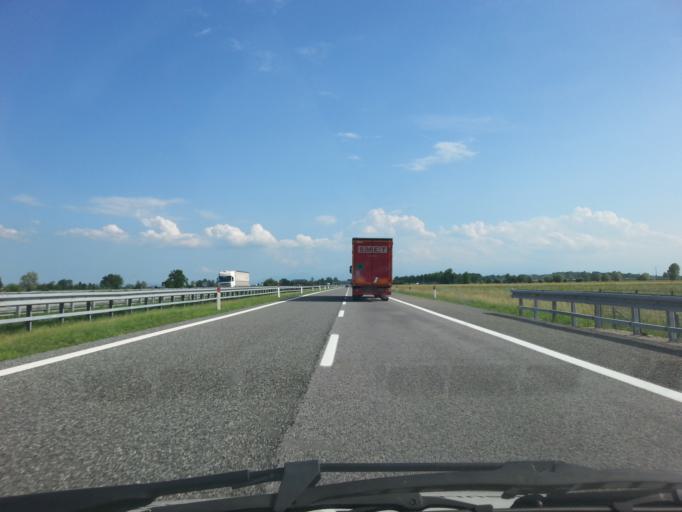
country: IT
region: Piedmont
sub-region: Provincia di Cuneo
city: Marene
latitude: 44.6878
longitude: 7.7677
